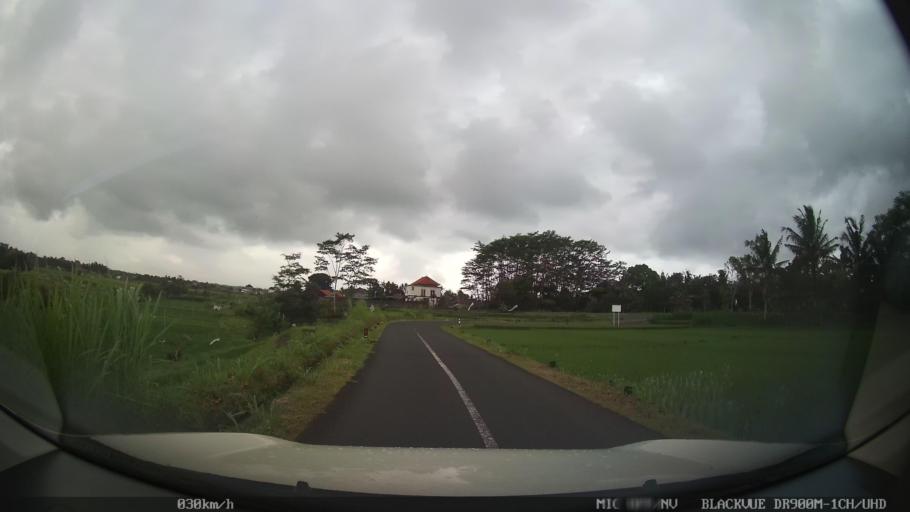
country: ID
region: Bali
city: Banjar Cemenggon
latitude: -8.5298
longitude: 115.1948
